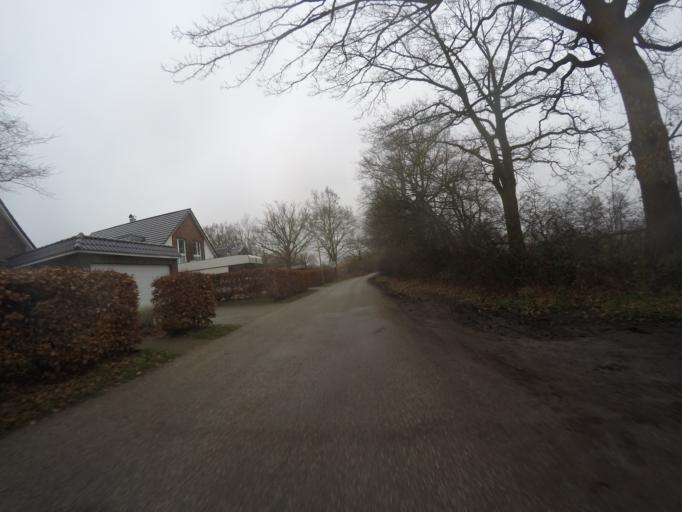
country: DE
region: Schleswig-Holstein
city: Quickborn
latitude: 53.7408
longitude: 9.8878
